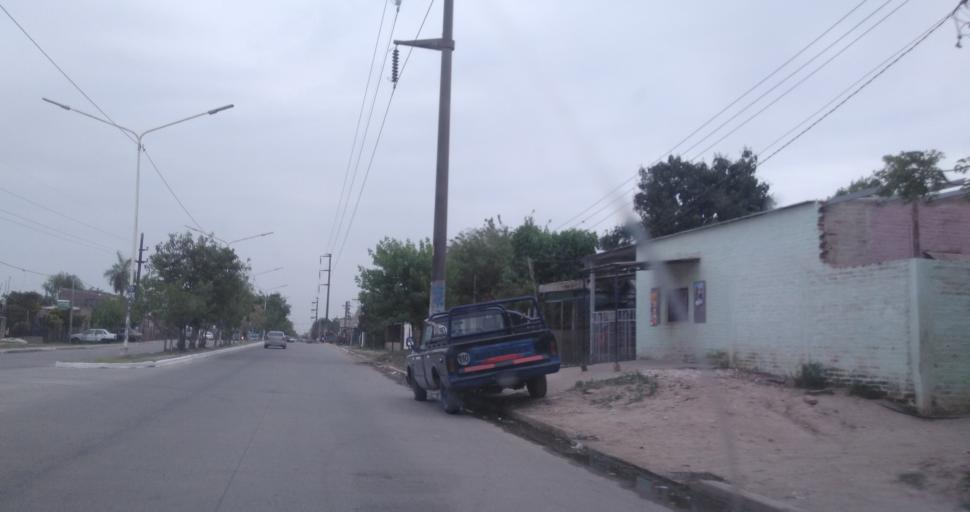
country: AR
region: Chaco
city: Fontana
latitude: -27.4208
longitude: -59.0206
